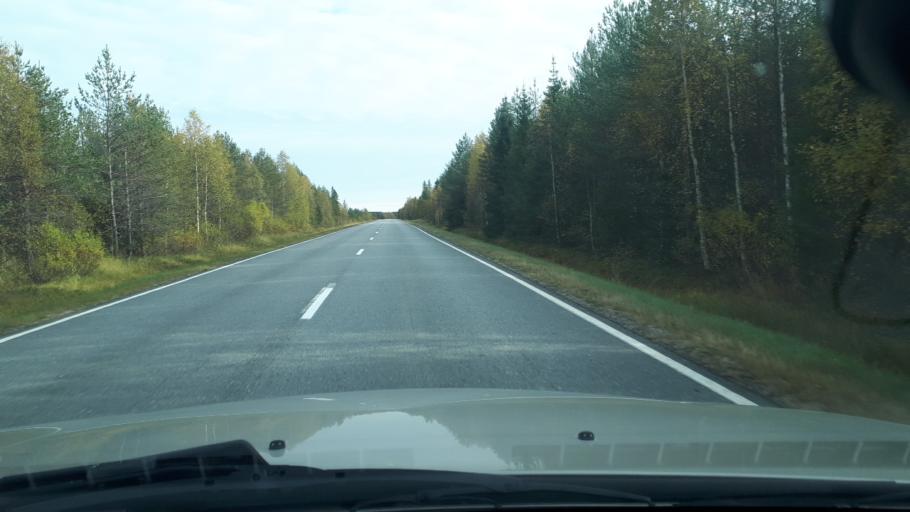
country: FI
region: Lapland
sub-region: Rovaniemi
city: Ranua
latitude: 65.9798
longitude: 26.1335
